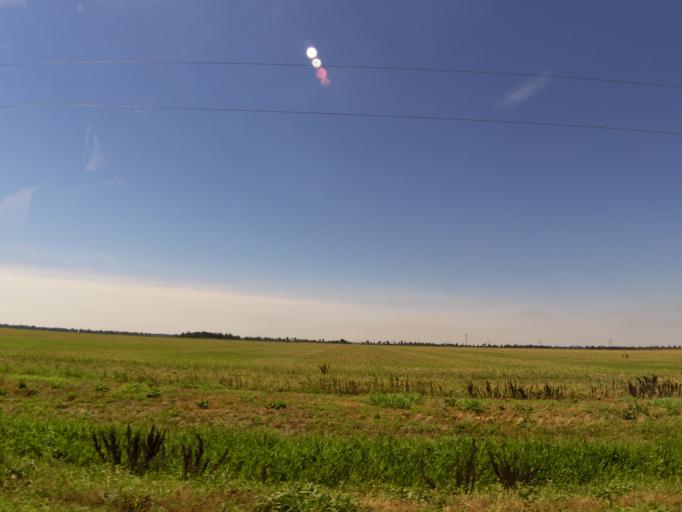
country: US
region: Missouri
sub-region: New Madrid County
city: Lilbourn
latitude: 36.5553
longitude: -89.6336
